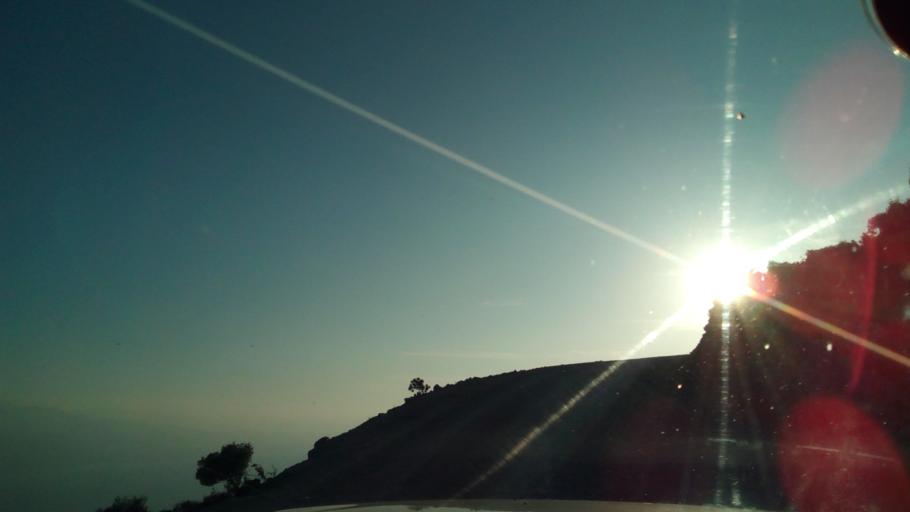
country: GR
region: West Greece
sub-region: Nomos Aitolias kai Akarnanias
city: Nafpaktos
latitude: 38.4340
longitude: 21.8515
